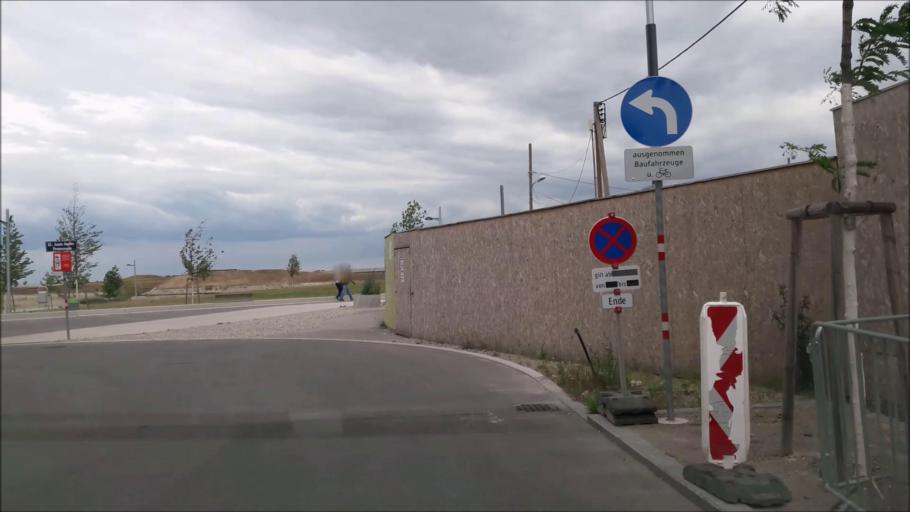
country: AT
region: Lower Austria
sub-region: Politischer Bezirk Ganserndorf
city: Gross-Enzersdorf
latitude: 48.2263
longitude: 16.5045
